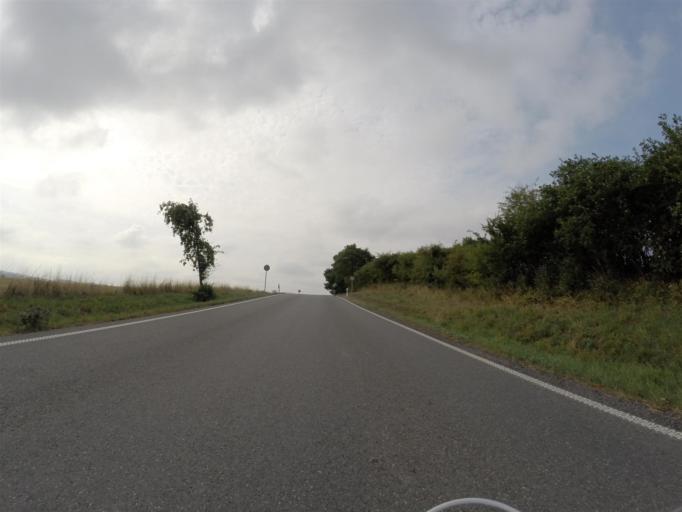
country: DE
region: Thuringia
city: Schongleina
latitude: 50.9131
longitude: 11.7314
